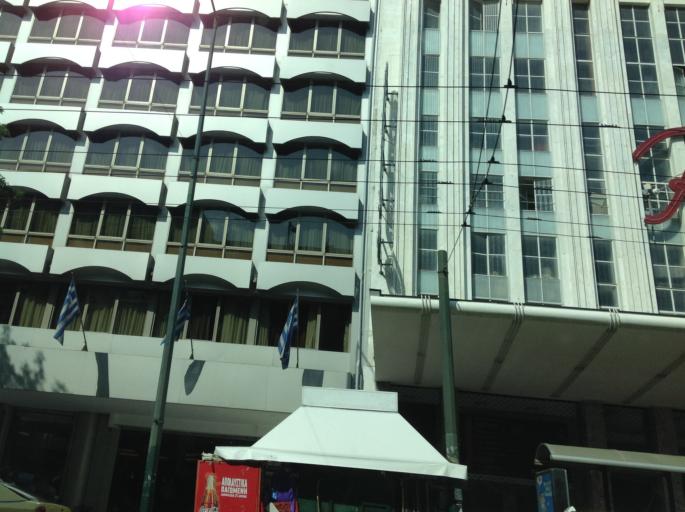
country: GR
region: Attica
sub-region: Nomarchia Athinas
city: Athens
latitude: 37.9827
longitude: 23.7310
